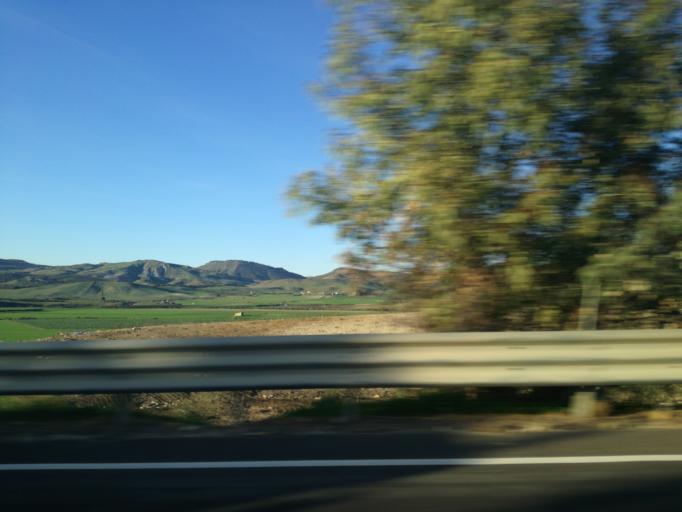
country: IT
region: Sicily
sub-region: Provincia di Caltanissetta
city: Niscemi
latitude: 37.2114
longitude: 14.3988
